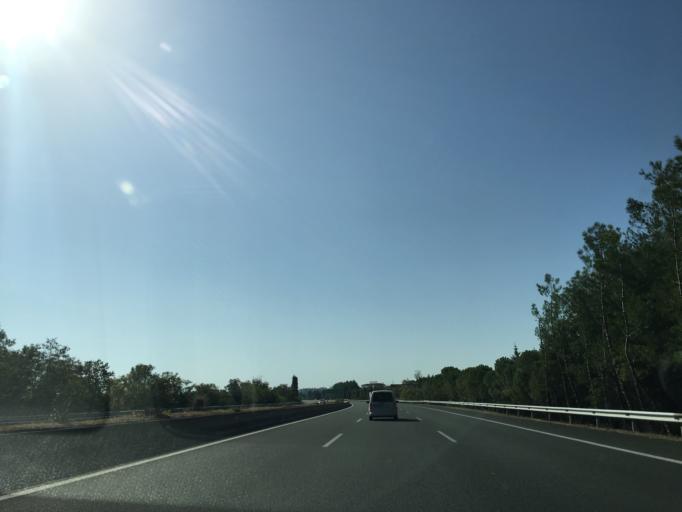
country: GR
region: Central Macedonia
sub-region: Nomos Pierias
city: Aiginio
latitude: 40.4750
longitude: 22.5709
